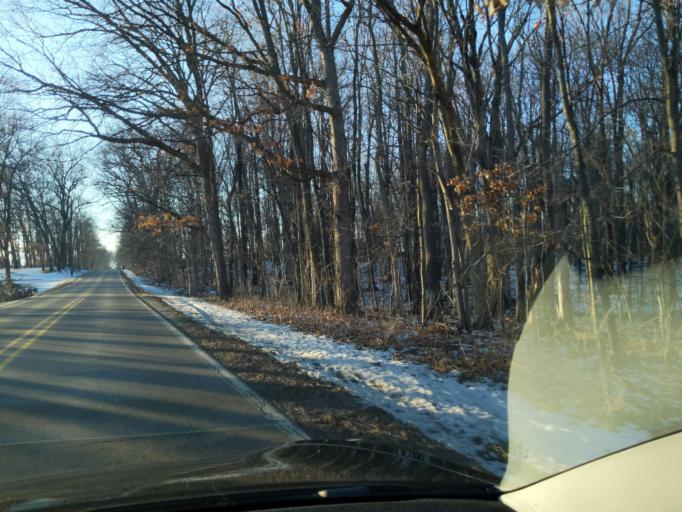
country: US
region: Michigan
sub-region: Ingham County
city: Stockbridge
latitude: 42.4678
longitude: -84.0908
